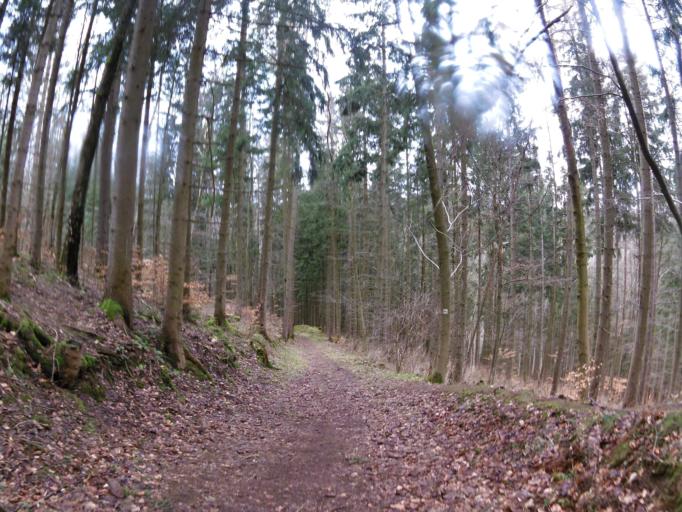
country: DE
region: Thuringia
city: Ilmenau
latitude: 50.6729
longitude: 10.9068
